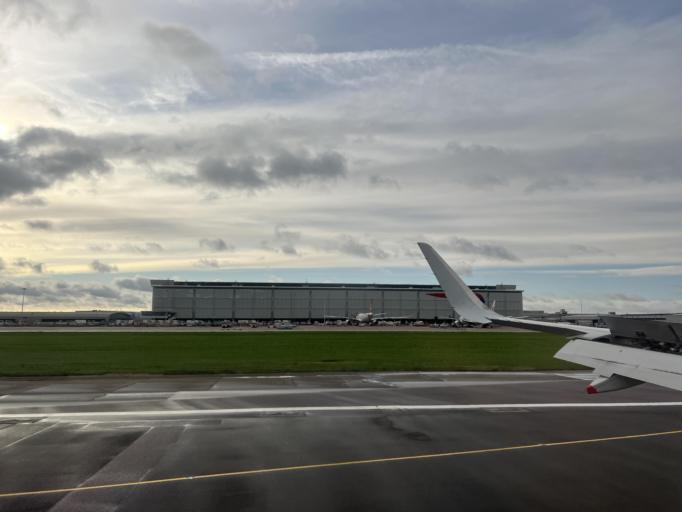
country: GB
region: England
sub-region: Greater London
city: West Drayton
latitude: 51.4645
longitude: -0.4642
